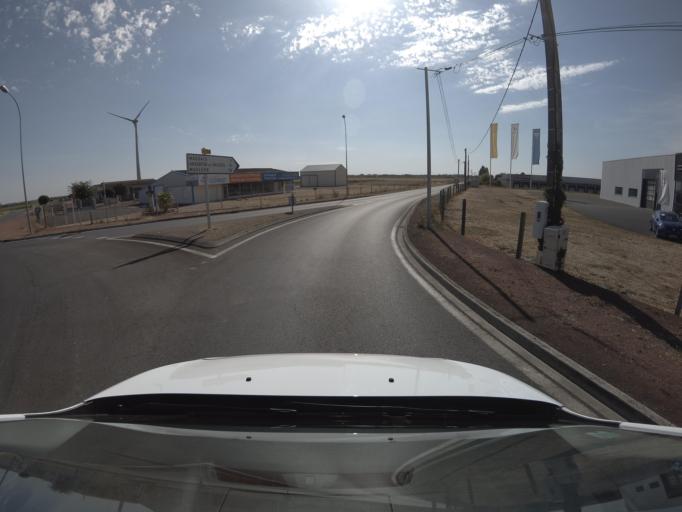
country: FR
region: Poitou-Charentes
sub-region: Departement des Deux-Sevres
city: Mauze-Thouarsais
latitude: 46.9988
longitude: -0.2847
